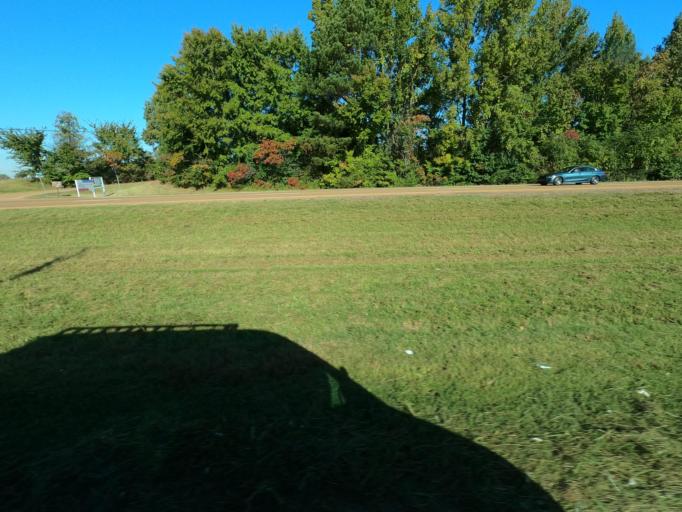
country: US
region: Tennessee
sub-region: Shelby County
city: Millington
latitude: 35.3829
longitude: -89.8645
